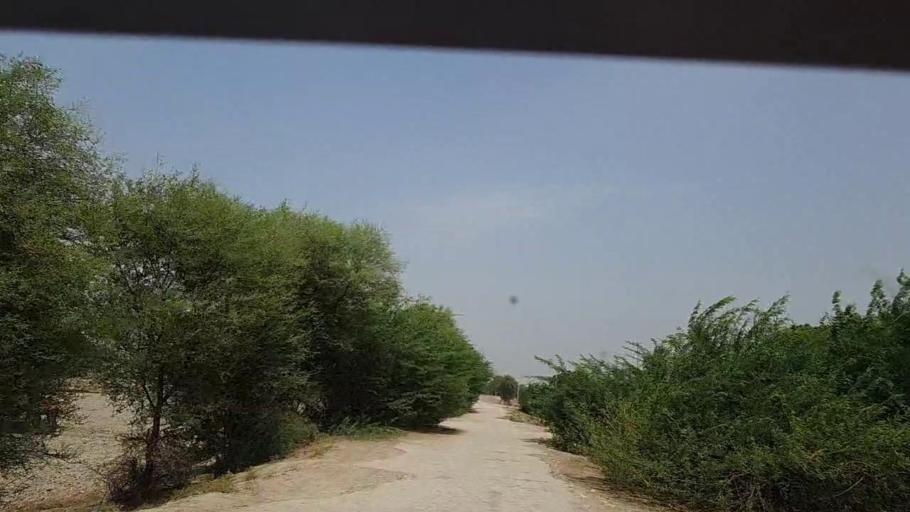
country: PK
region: Sindh
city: Khairpur Nathan Shah
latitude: 27.0810
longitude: 67.6697
